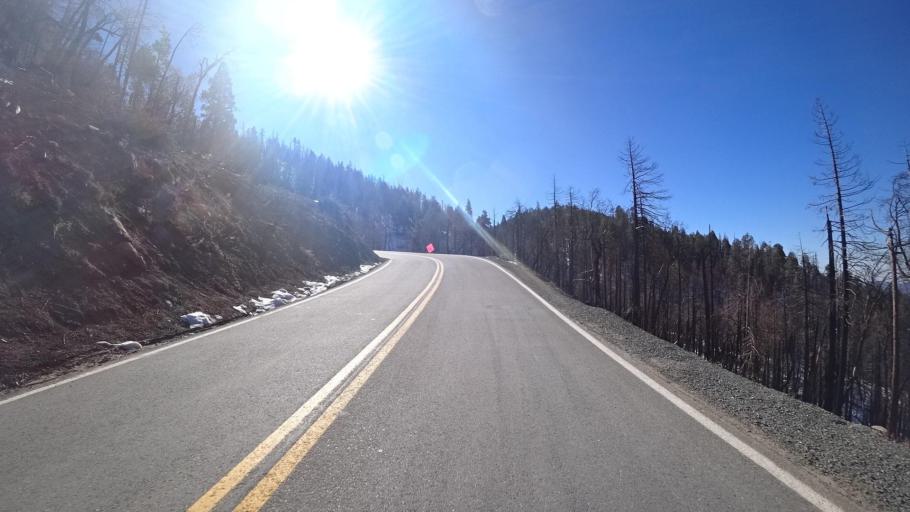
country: US
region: California
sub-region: Kern County
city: Alta Sierra
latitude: 35.7470
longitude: -118.5563
